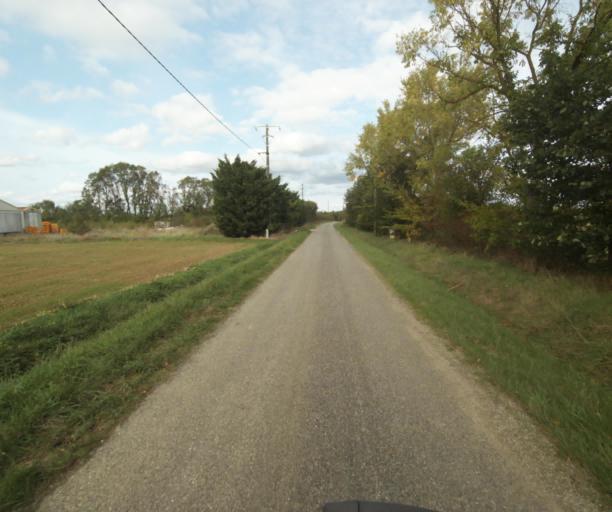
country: FR
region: Midi-Pyrenees
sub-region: Departement du Tarn-et-Garonne
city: Verdun-sur-Garonne
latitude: 43.8456
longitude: 1.1657
